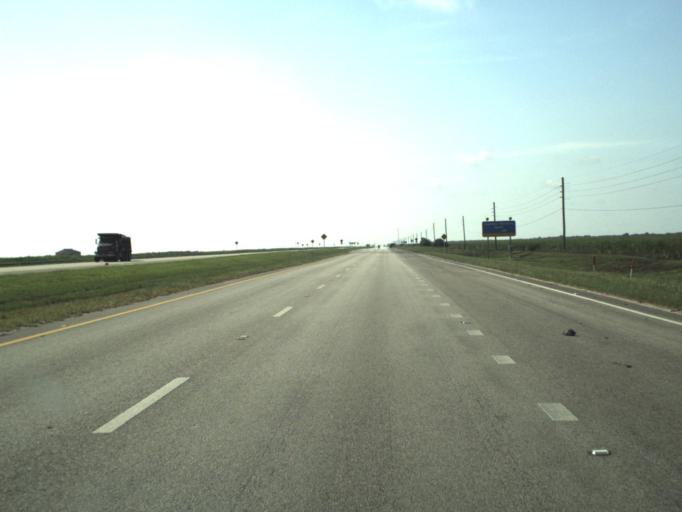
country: US
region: Florida
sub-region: Palm Beach County
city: Belle Glade Camp
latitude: 26.5405
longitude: -80.6974
